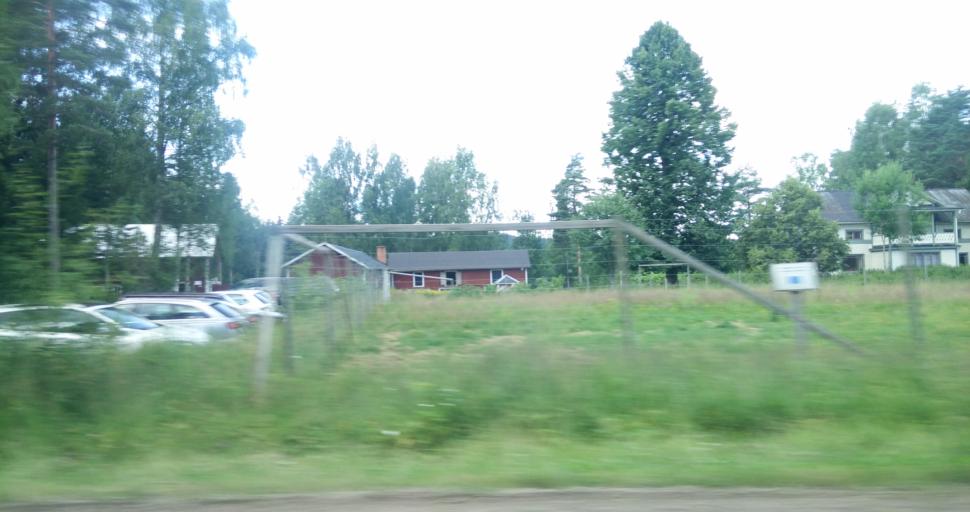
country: SE
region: Vaermland
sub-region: Hagfors Kommun
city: Ekshaerad
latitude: 60.1099
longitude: 13.4494
